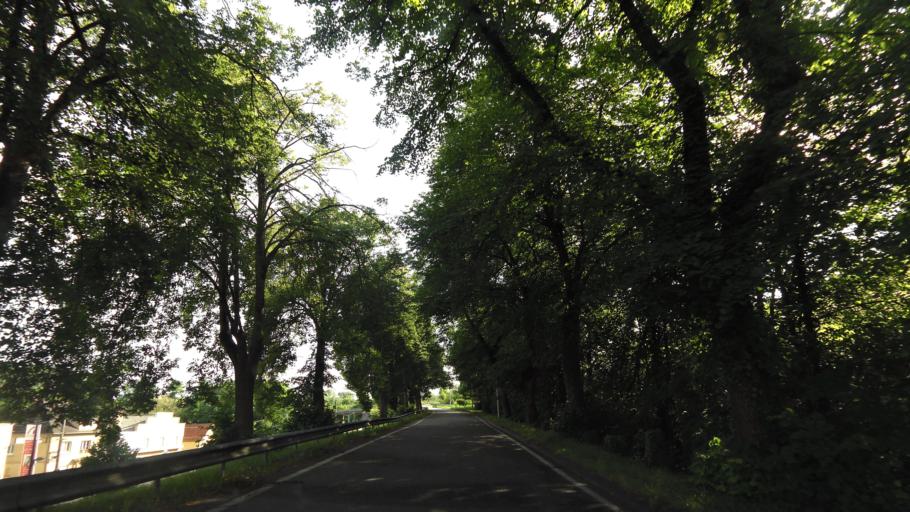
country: FR
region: Lorraine
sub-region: Departement de la Moselle
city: Sarrebourg
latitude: 48.7313
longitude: 7.0391
